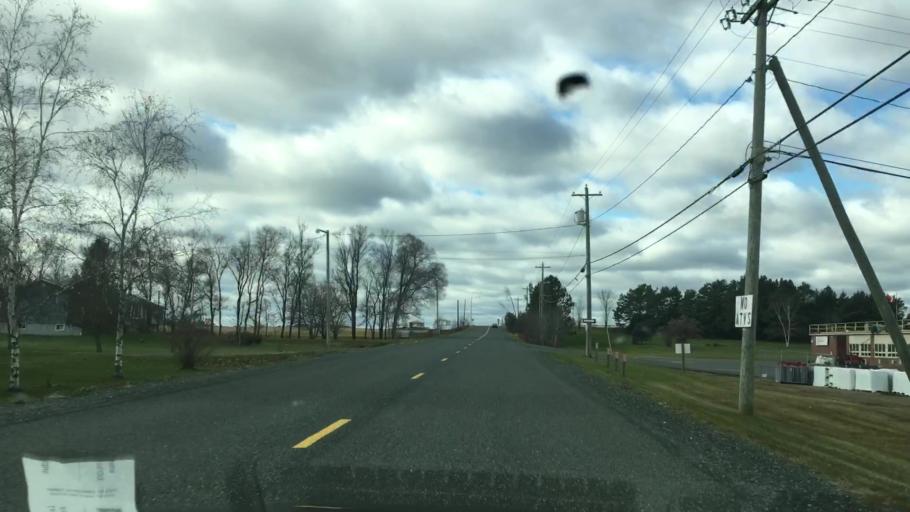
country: CA
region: New Brunswick
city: Florenceville-Bristol
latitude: 46.2882
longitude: -67.5449
